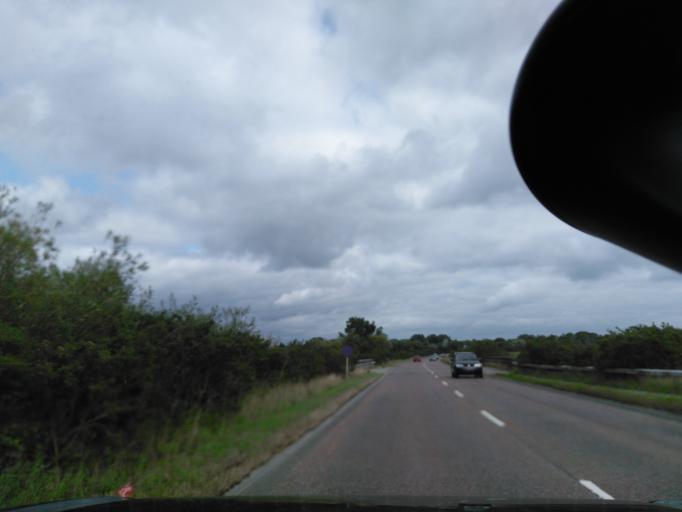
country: GB
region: England
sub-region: Dorset
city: Wareham
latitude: 50.6882
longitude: -2.1206
